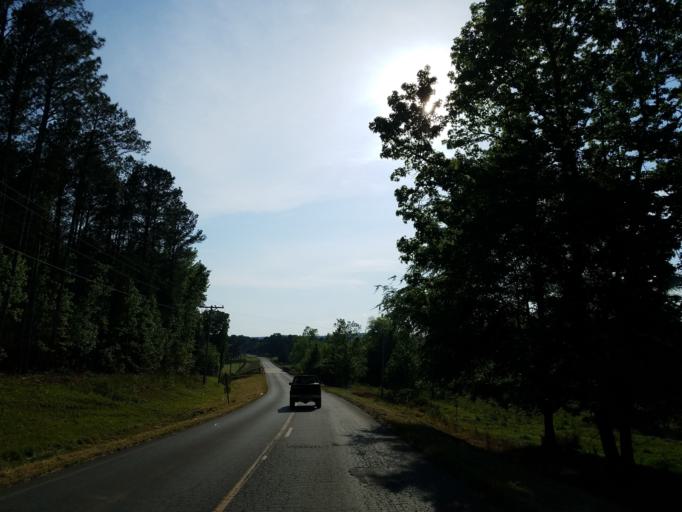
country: US
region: Georgia
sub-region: Chattooga County
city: Trion
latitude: 34.5692
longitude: -85.1590
